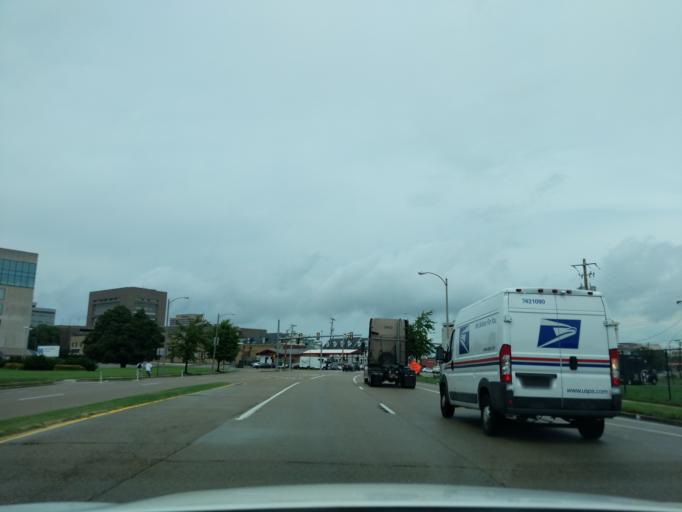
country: US
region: Tennessee
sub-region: Shelby County
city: Memphis
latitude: 35.1452
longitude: -90.0439
